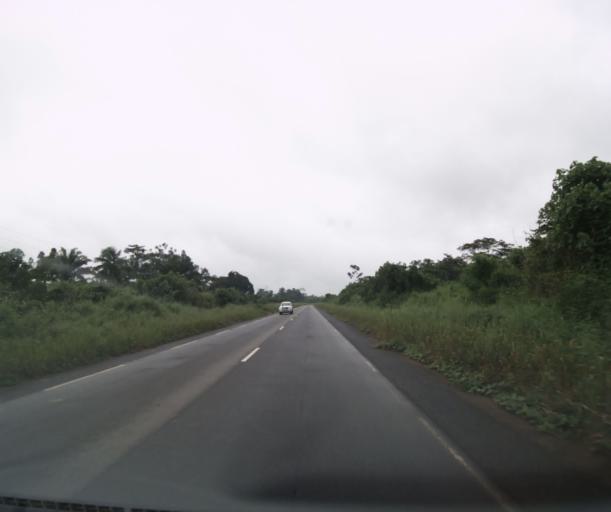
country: CM
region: Littoral
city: Edea
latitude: 3.4827
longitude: 10.1293
